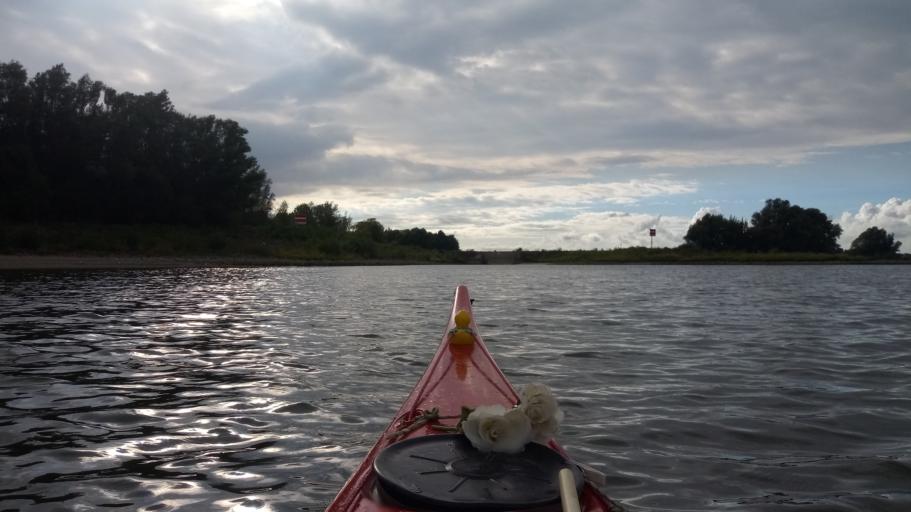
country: NL
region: Gelderland
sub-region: Gemeente Neerijnen
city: Neerijnen
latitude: 51.8177
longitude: 5.3223
